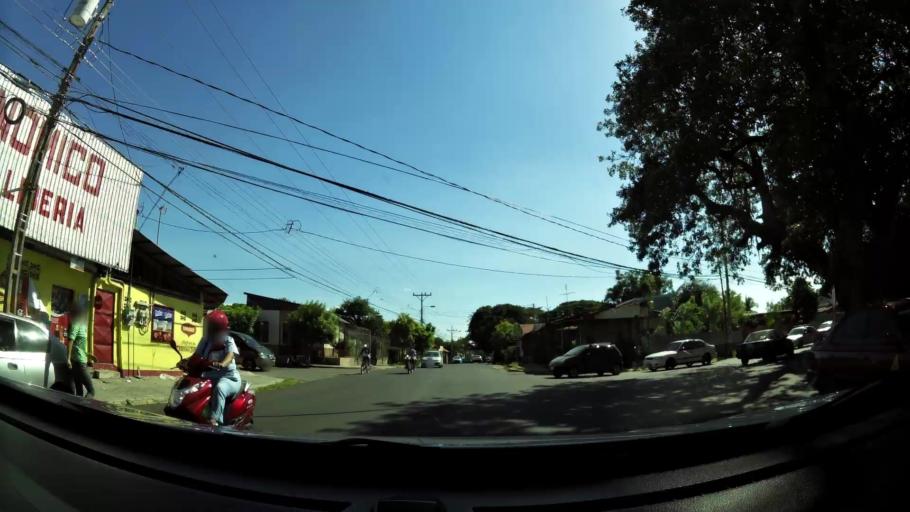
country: CR
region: Guanacaste
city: Liberia
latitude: 10.6350
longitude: -85.4326
